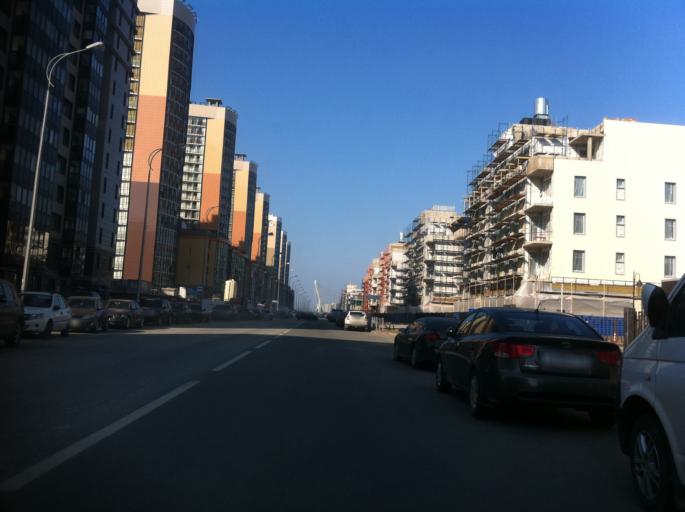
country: RU
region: St.-Petersburg
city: Sosnovaya Polyana
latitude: 59.8486
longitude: 30.1558
